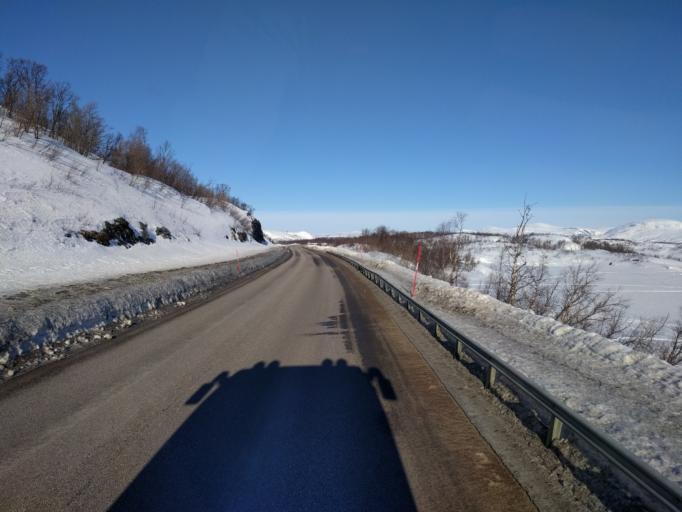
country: NO
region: Troms
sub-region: Bardu
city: Setermoen
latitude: 68.4332
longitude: 18.6618
